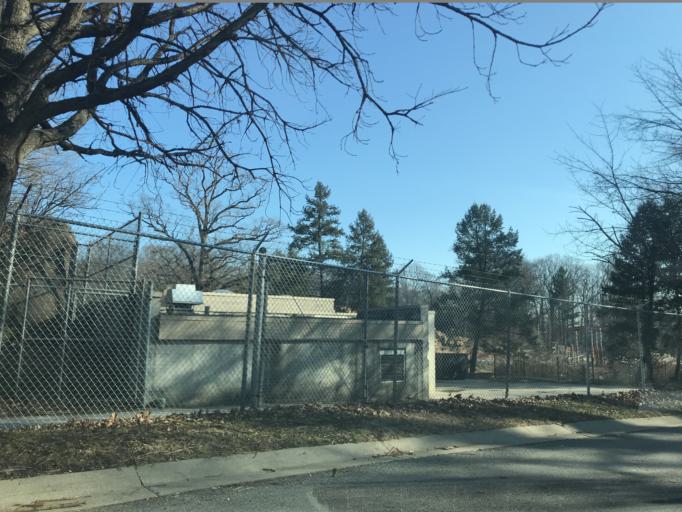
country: US
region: Maryland
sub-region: City of Baltimore
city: Baltimore
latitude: 39.3243
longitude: -76.6439
